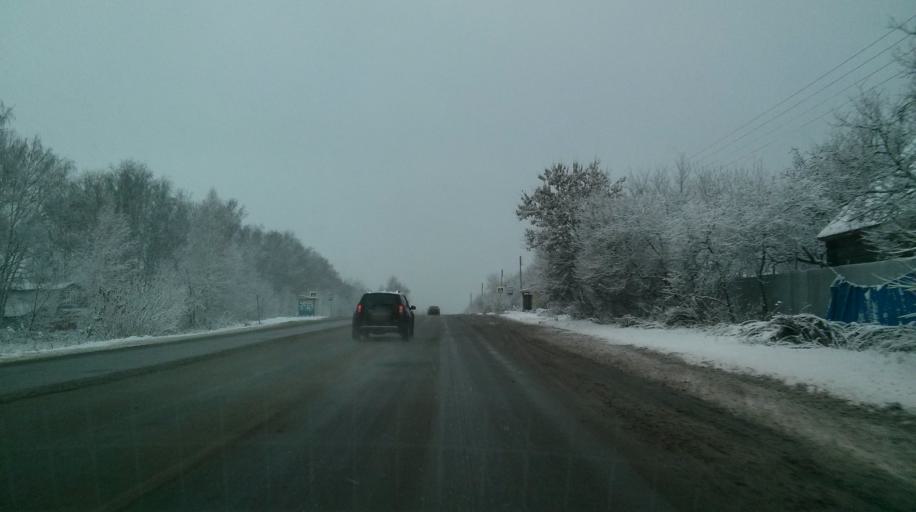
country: RU
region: Nizjnij Novgorod
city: Burevestnik
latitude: 56.1825
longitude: 43.7994
